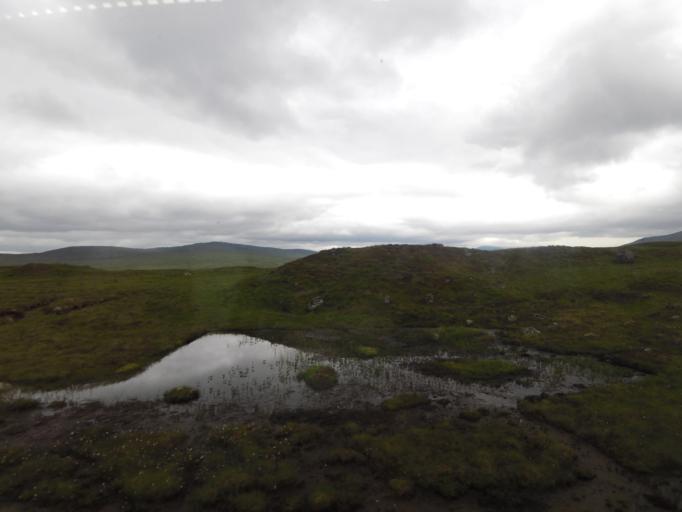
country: GB
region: Scotland
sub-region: Highland
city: Spean Bridge
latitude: 56.7259
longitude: -4.6377
